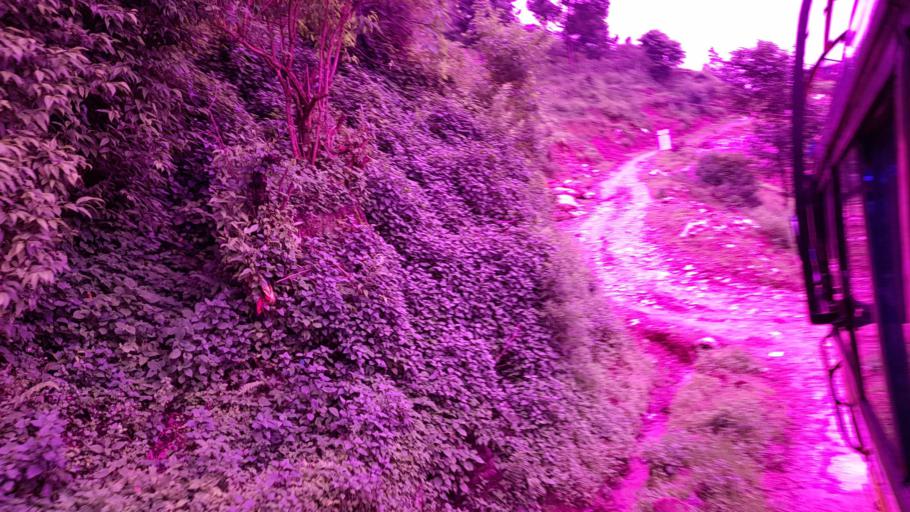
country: NP
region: Central Region
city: Kirtipur
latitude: 27.8227
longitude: 85.2103
